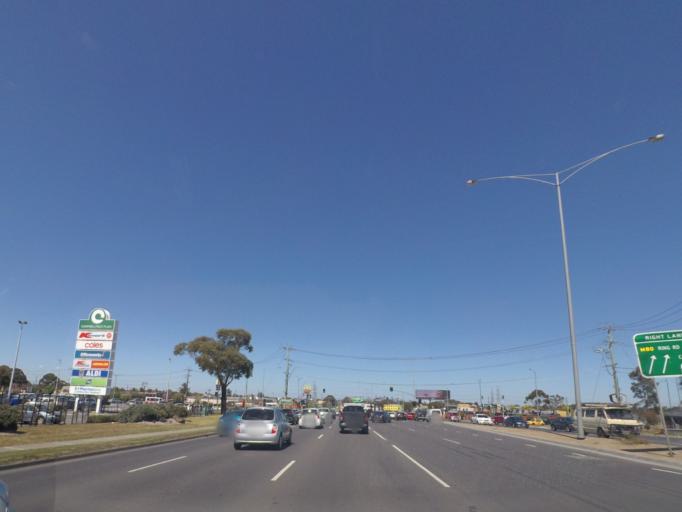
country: AU
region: Victoria
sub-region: Hume
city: Campbellfield
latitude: -37.6885
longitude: 144.9581
